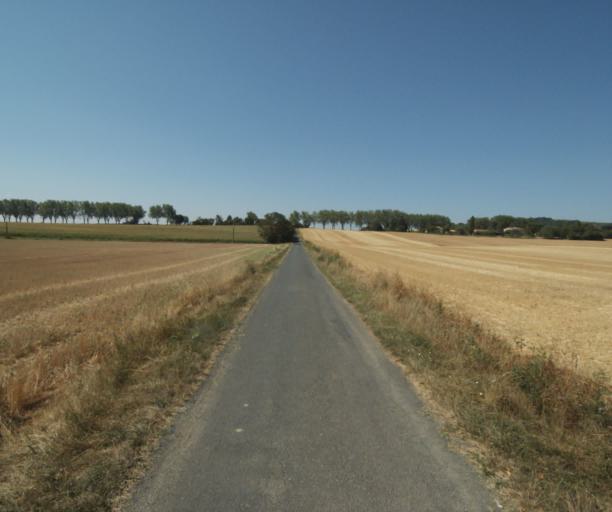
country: FR
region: Midi-Pyrenees
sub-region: Departement de la Haute-Garonne
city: Revel
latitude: 43.5048
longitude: 1.9558
